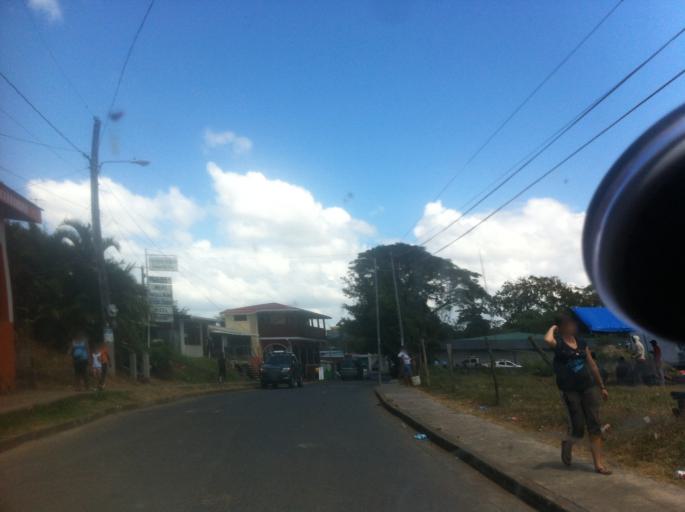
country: NI
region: Rio San Juan
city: San Carlos
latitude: 11.1258
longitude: -84.7776
